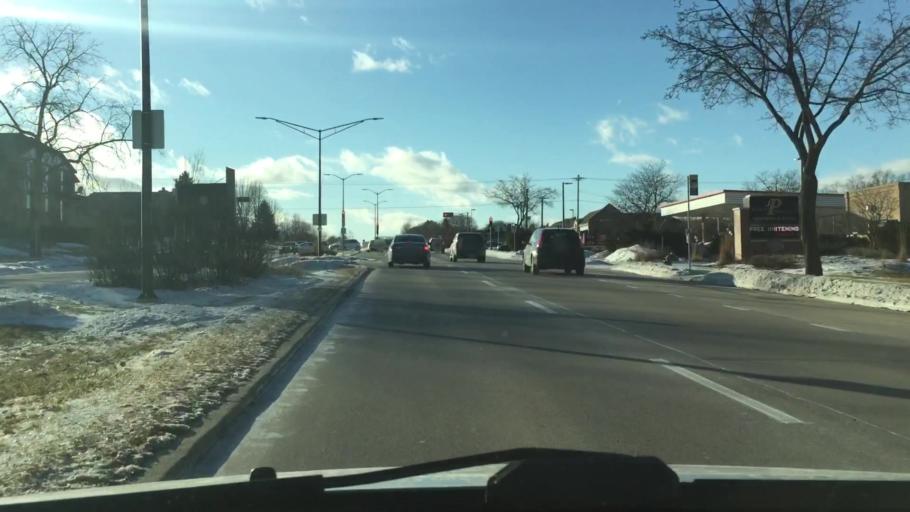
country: US
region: Wisconsin
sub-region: Waukesha County
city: New Berlin
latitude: 42.9883
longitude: -88.0669
